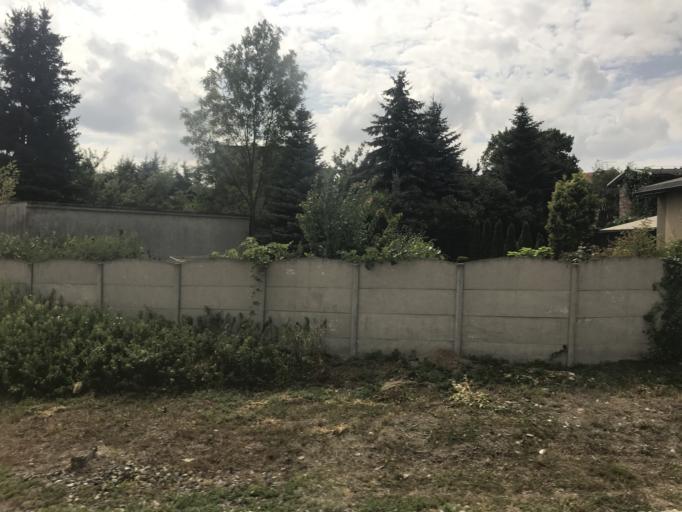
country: PL
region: Greater Poland Voivodeship
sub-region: Powiat poznanski
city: Pobiedziska
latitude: 52.4805
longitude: 17.2836
